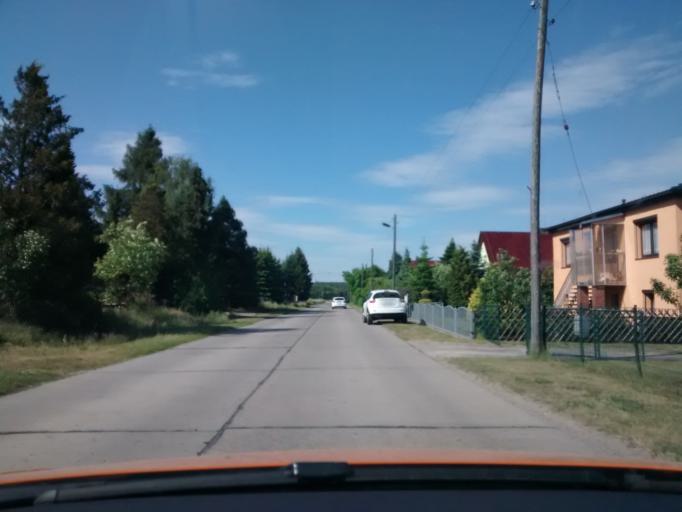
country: DE
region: Brandenburg
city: Juterbog
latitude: 51.9783
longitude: 13.1713
